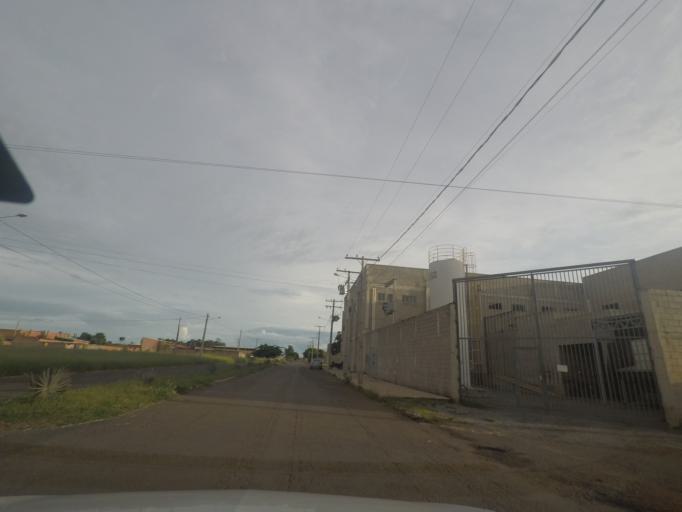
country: BR
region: Goias
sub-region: Trindade
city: Trindade
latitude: -16.7262
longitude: -49.4394
